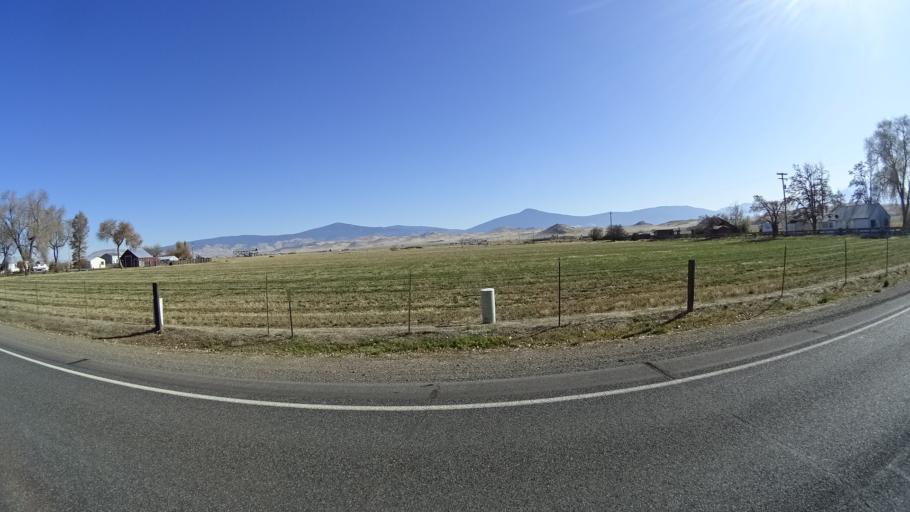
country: US
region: California
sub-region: Siskiyou County
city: Montague
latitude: 41.7570
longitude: -122.5248
